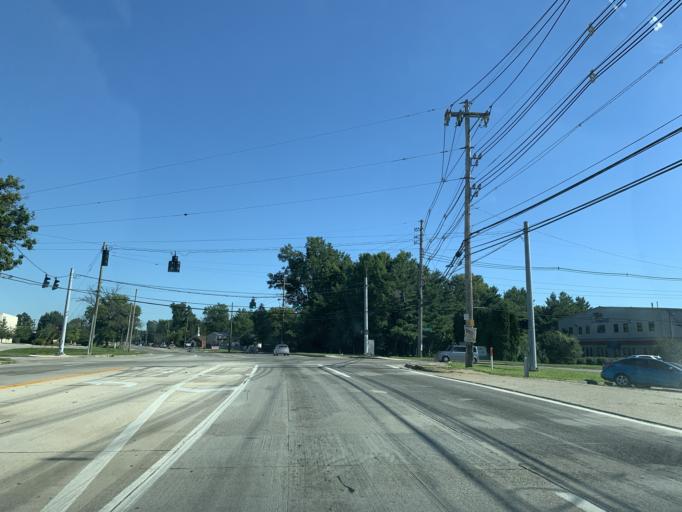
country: US
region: Kentucky
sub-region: Jefferson County
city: Audubon Park
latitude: 38.1831
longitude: -85.6987
